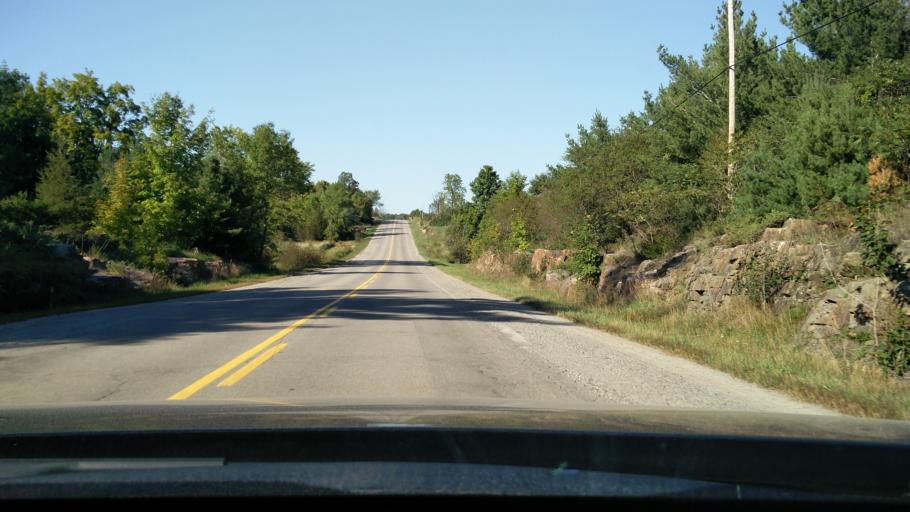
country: CA
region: Ontario
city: Perth
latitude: 44.7221
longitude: -76.4000
